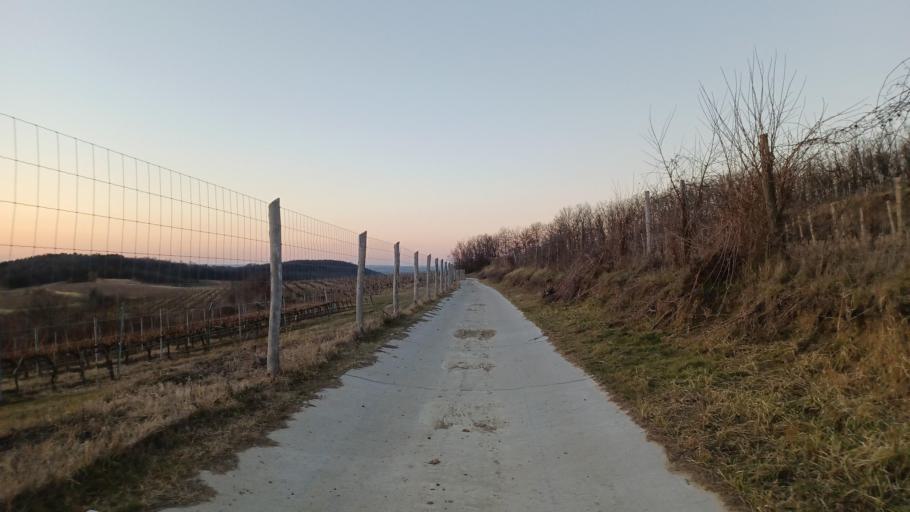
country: HU
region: Tolna
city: Szentgalpuszta
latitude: 46.3430
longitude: 18.6412
